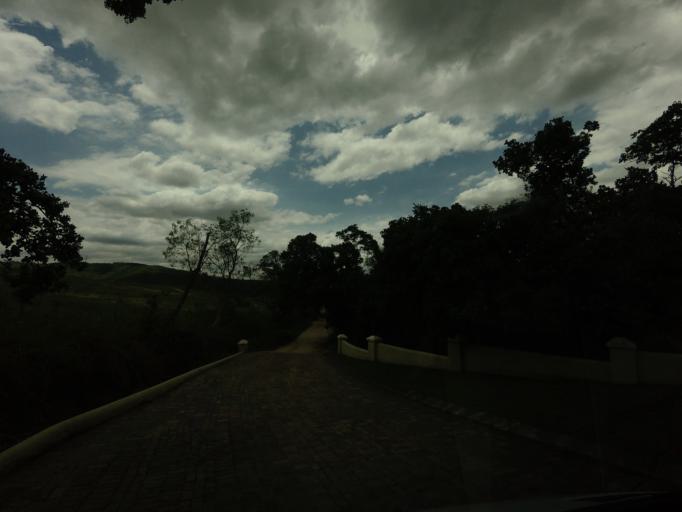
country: ZA
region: Mpumalanga
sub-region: Ehlanzeni District
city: Graksop
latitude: -25.0461
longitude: 31.0790
